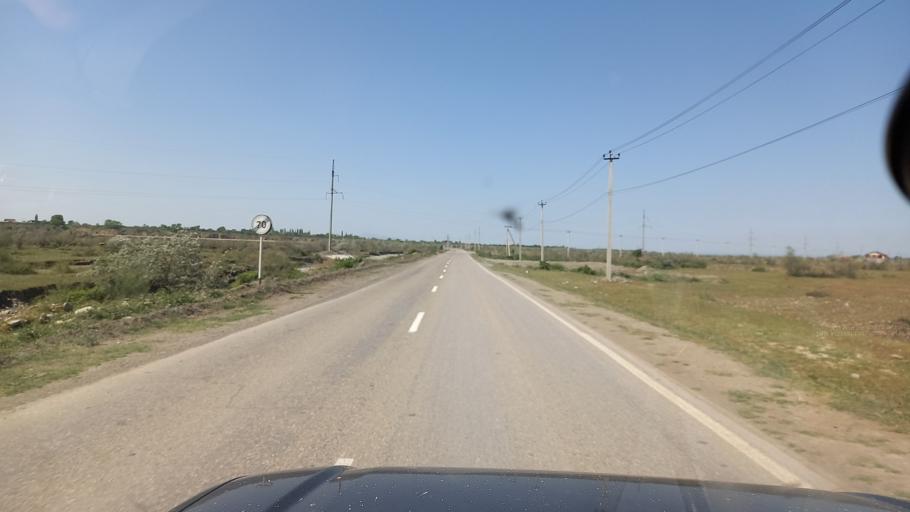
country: AZ
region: Qusar
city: Samur
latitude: 41.7309
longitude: 48.4538
